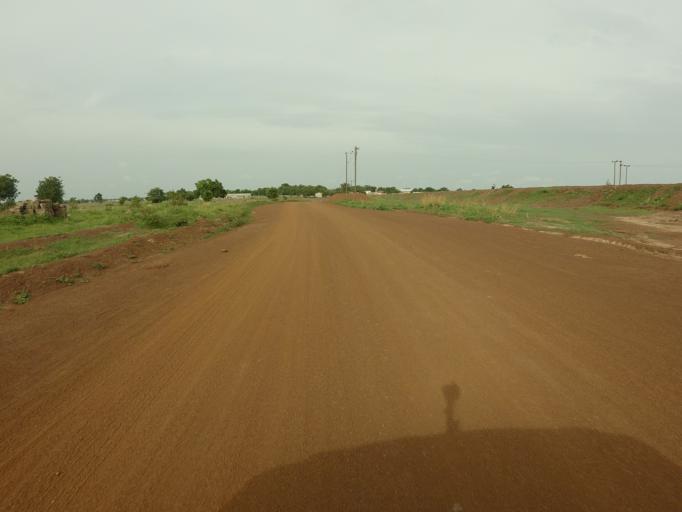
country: GH
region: Northern
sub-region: Yendi
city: Yendi
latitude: 9.9291
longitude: -0.2079
